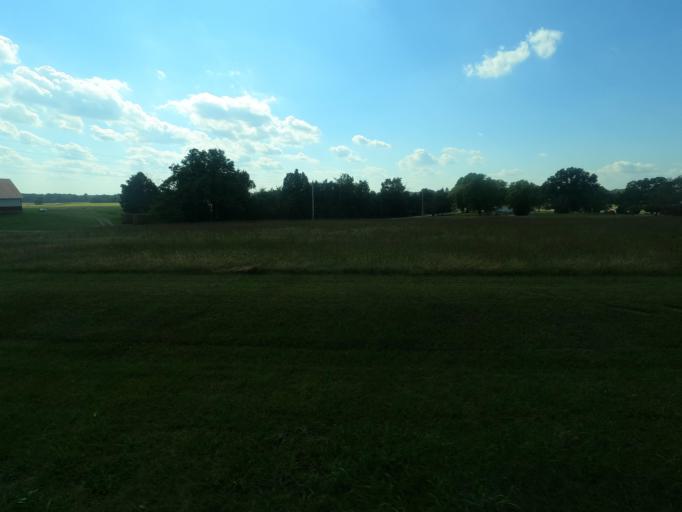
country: US
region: Illinois
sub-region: Massac County
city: Metropolis
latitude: 37.2212
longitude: -88.7296
